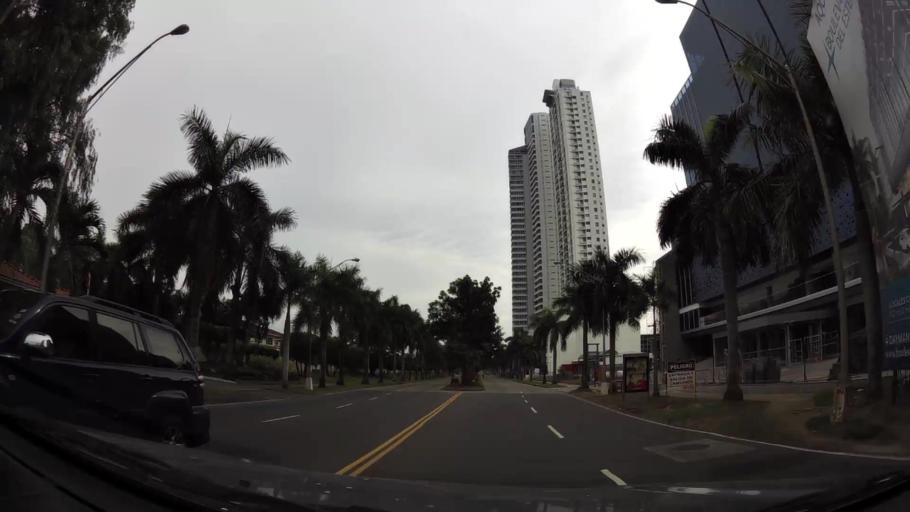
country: PA
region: Panama
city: San Miguelito
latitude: 9.0164
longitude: -79.4691
